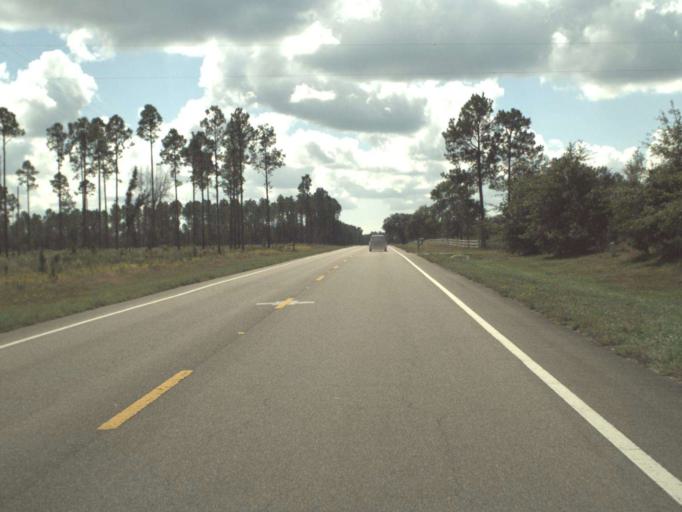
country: US
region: Florida
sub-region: Walton County
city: Freeport
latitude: 30.5118
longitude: -85.9265
